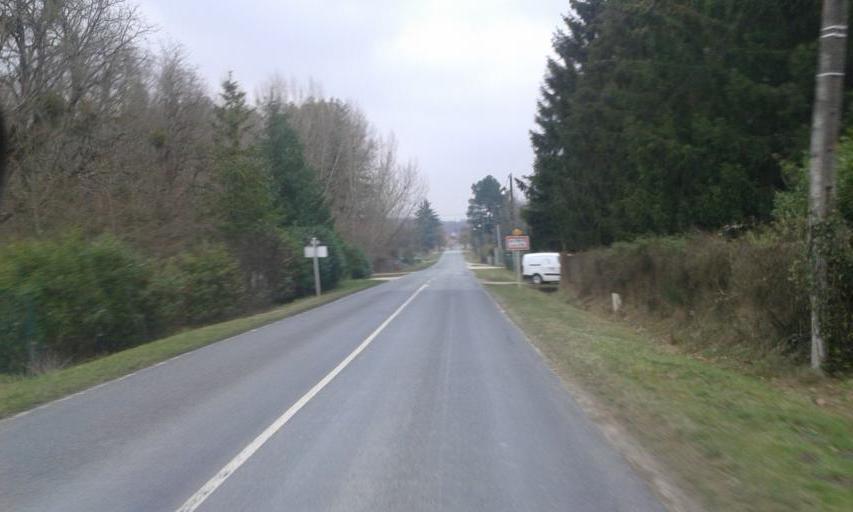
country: FR
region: Centre
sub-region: Departement du Loir-et-Cher
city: Dhuizon
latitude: 47.6492
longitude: 1.6689
